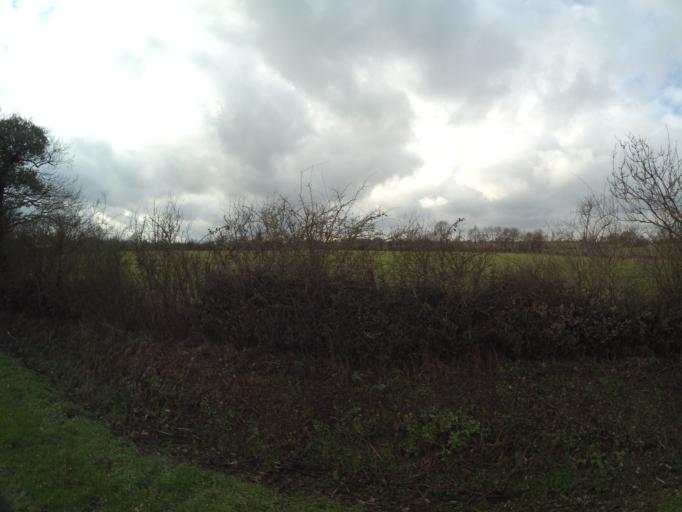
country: FR
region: Pays de la Loire
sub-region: Departement de la Loire-Atlantique
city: Saint-Hilaire-de-Clisson
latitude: 47.0357
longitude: -1.2932
